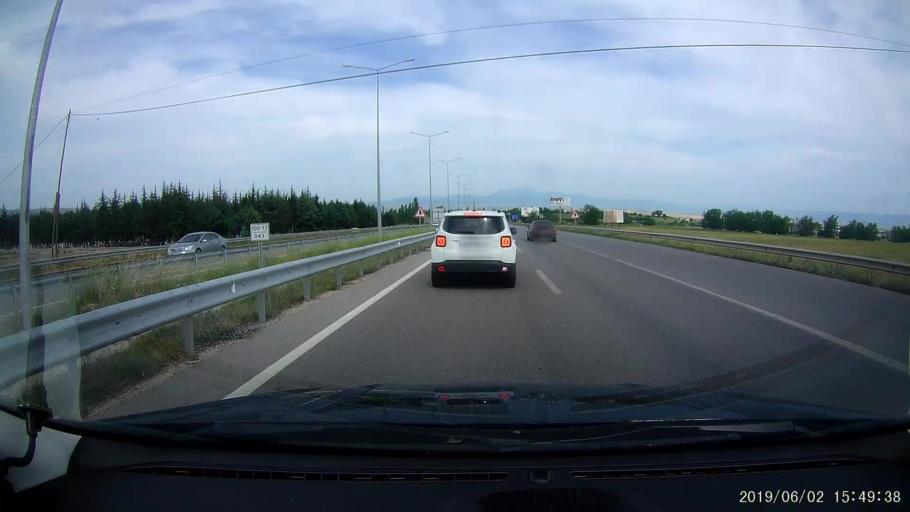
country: TR
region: Amasya
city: Merzifon
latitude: 40.8574
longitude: 35.4659
